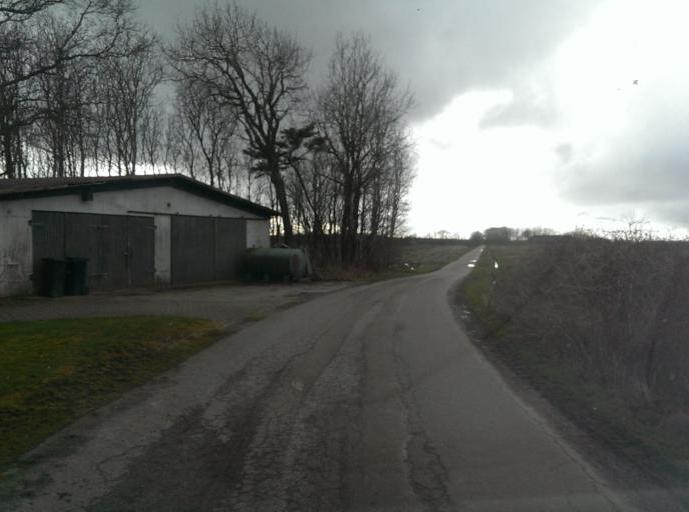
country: DK
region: South Denmark
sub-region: Esbjerg Kommune
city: Bramming
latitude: 55.4423
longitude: 8.6766
